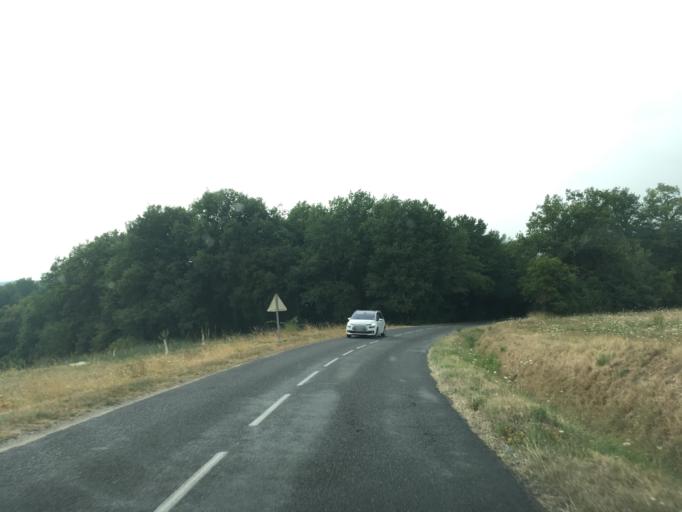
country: FR
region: Midi-Pyrenees
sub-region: Departement du Lot
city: Souillac
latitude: 44.8463
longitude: 1.5434
